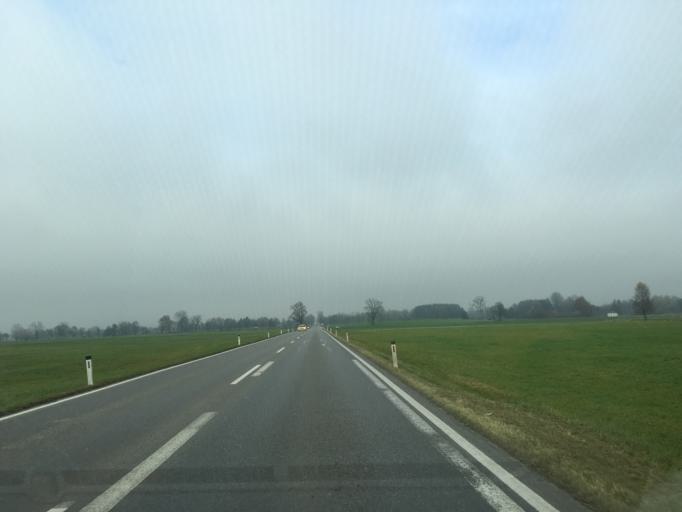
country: CH
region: Saint Gallen
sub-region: Wahlkreis Rheintal
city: Diepoldsau
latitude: 47.4001
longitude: 9.6767
